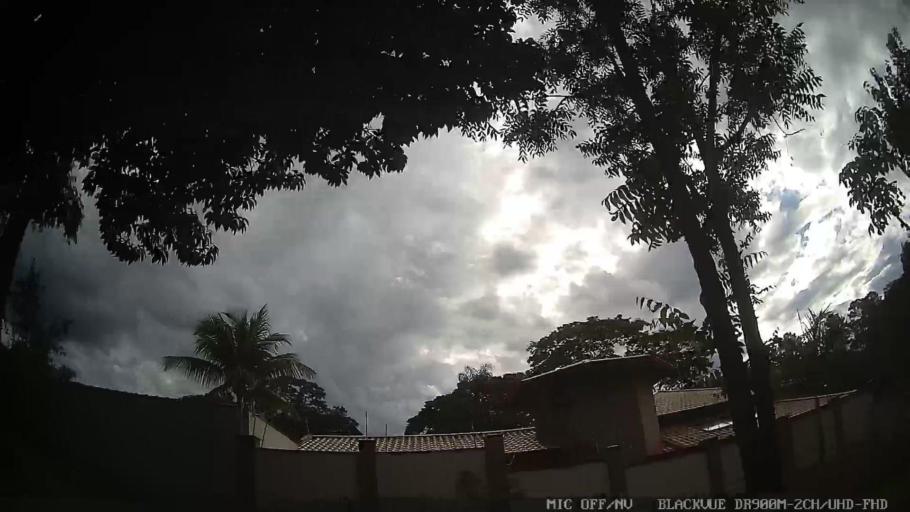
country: BR
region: Sao Paulo
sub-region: Jaguariuna
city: Jaguariuna
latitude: -22.6828
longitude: -47.0009
